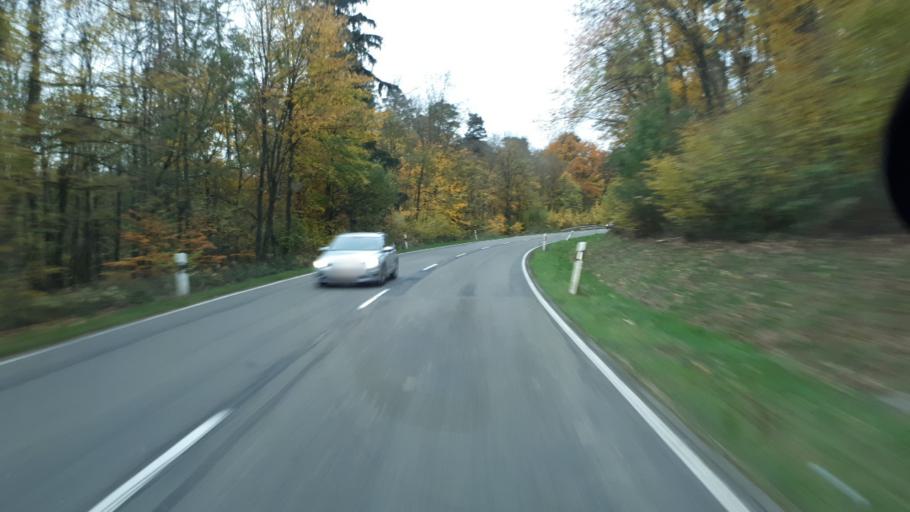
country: DE
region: Rheinland-Pfalz
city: Kaisersesch
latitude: 50.2162
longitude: 7.1433
